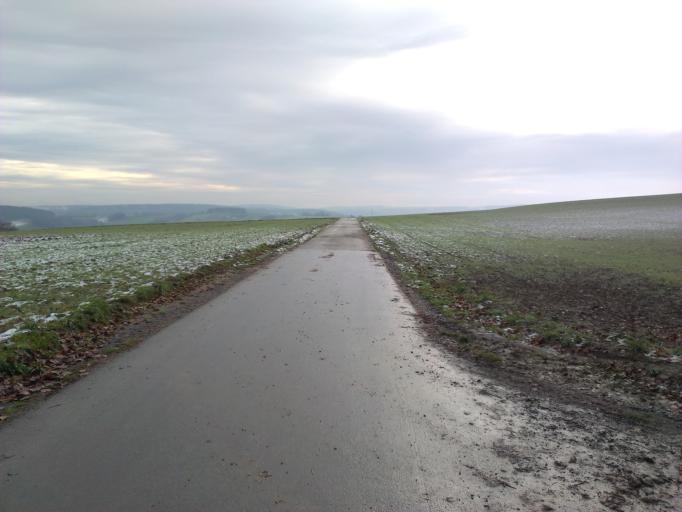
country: DE
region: Baden-Wuerttemberg
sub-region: Karlsruhe Region
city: Balzfeld
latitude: 49.2587
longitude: 8.7674
